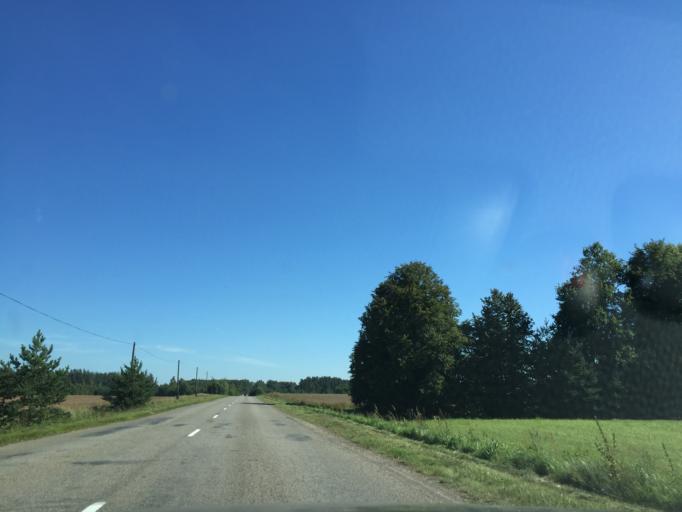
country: LV
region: Akniste
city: Akniste
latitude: 56.1446
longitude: 25.7982
